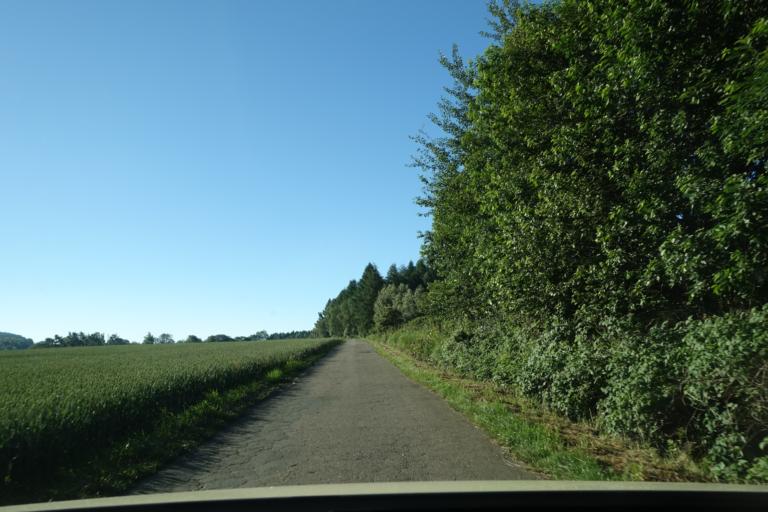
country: DE
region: Saxony
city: Eppendorf
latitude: 50.7785
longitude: 13.2442
